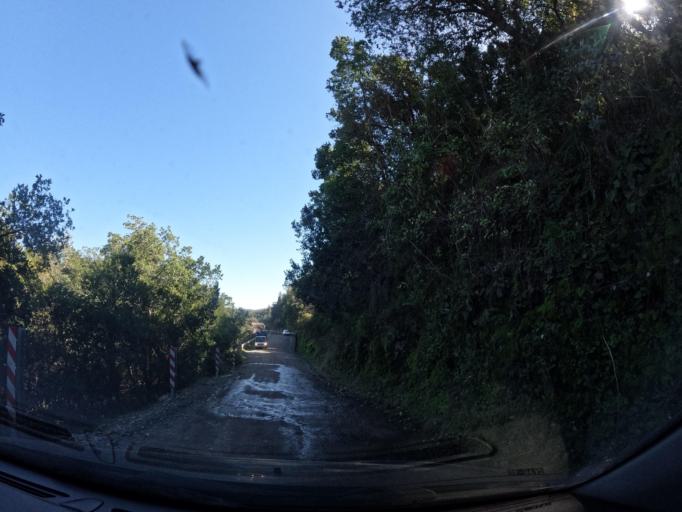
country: CL
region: Maule
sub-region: Provincia de Linares
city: Longavi
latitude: -36.2296
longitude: -71.4010
